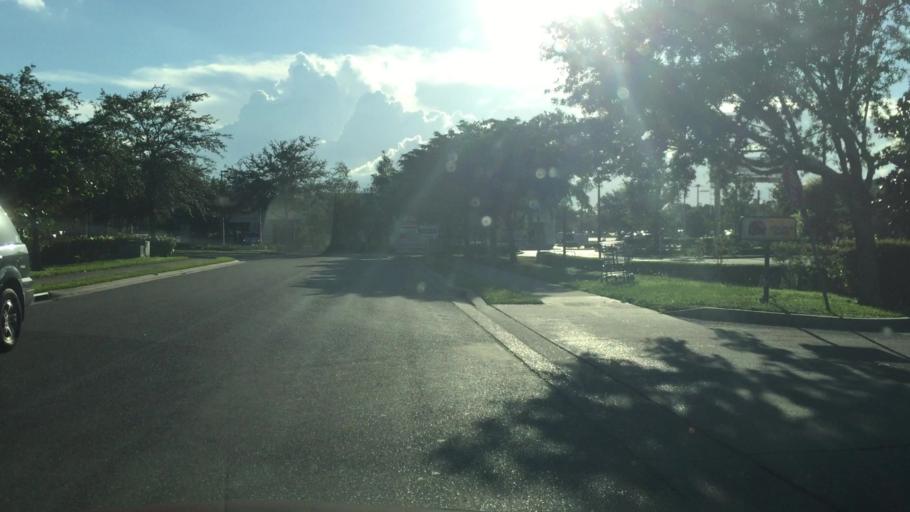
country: US
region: Florida
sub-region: Lee County
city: Fort Myers
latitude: 26.6116
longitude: -81.8094
